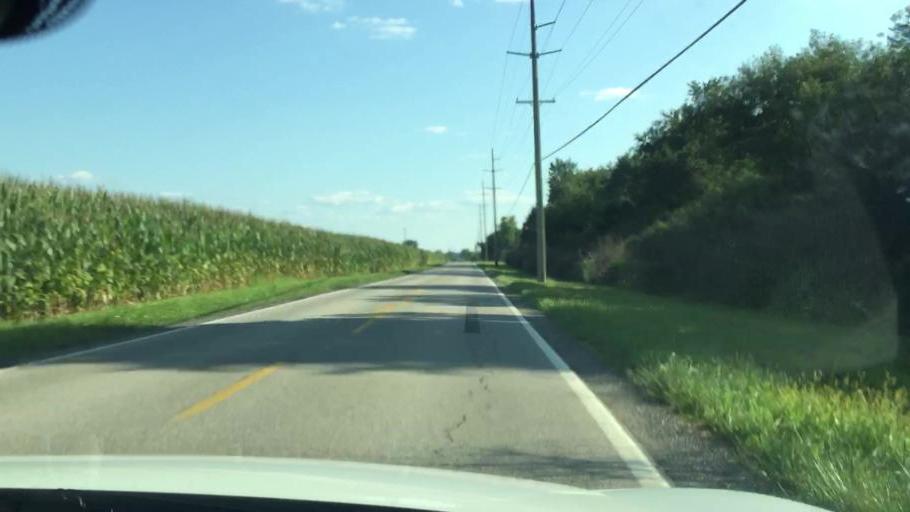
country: US
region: Ohio
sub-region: Clark County
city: Northridge
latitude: 39.9549
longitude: -83.7089
